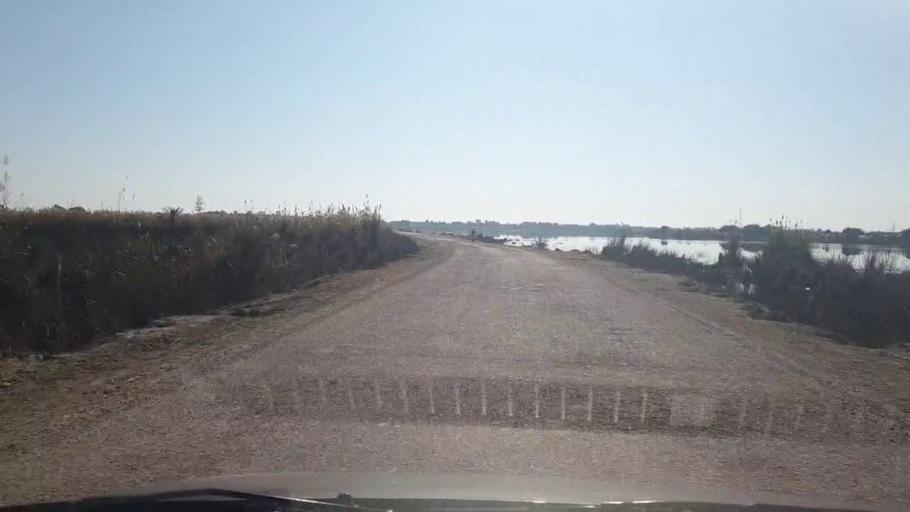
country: PK
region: Sindh
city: Bozdar
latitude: 27.1612
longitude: 68.6455
